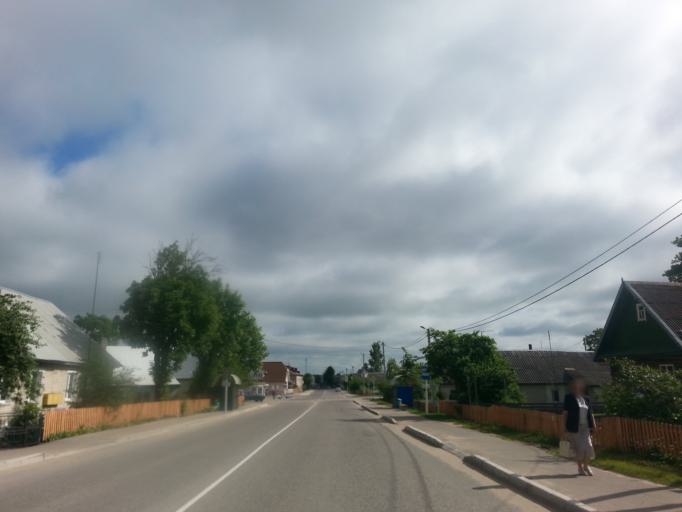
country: BY
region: Vitebsk
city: Hlybokaye
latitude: 55.1307
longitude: 27.6798
